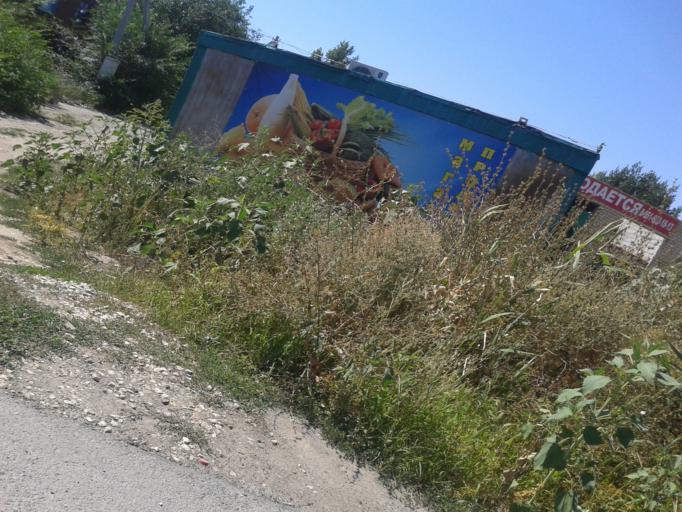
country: RU
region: Volgograd
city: Volgograd
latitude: 48.6910
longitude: 44.4447
